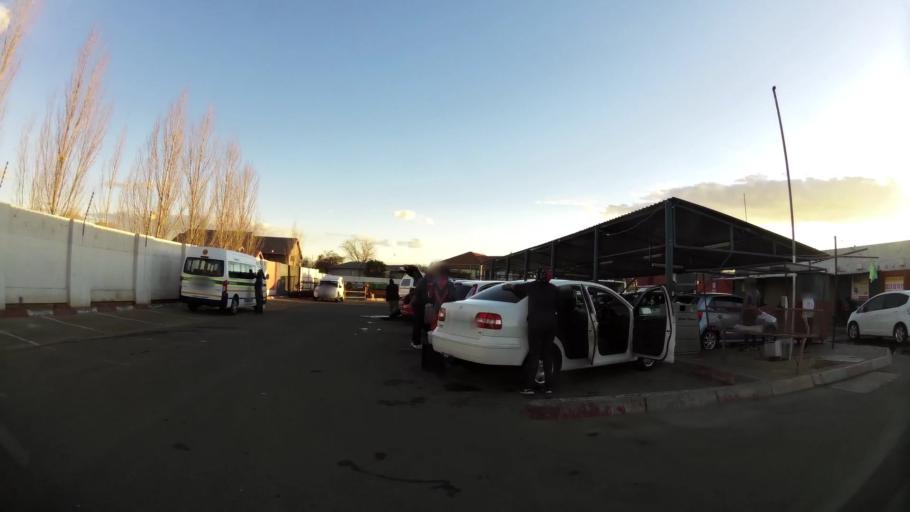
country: ZA
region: North-West
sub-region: Dr Kenneth Kaunda District Municipality
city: Potchefstroom
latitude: -26.7139
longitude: 27.1084
